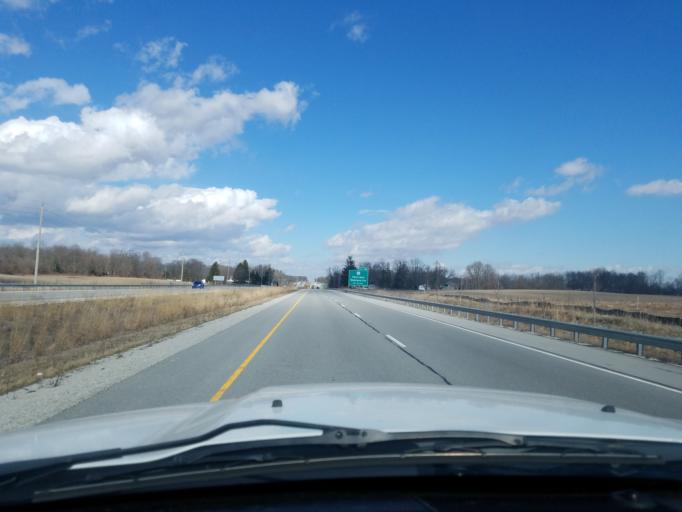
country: US
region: Indiana
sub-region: Hamilton County
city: Westfield
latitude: 40.0788
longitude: -86.1277
